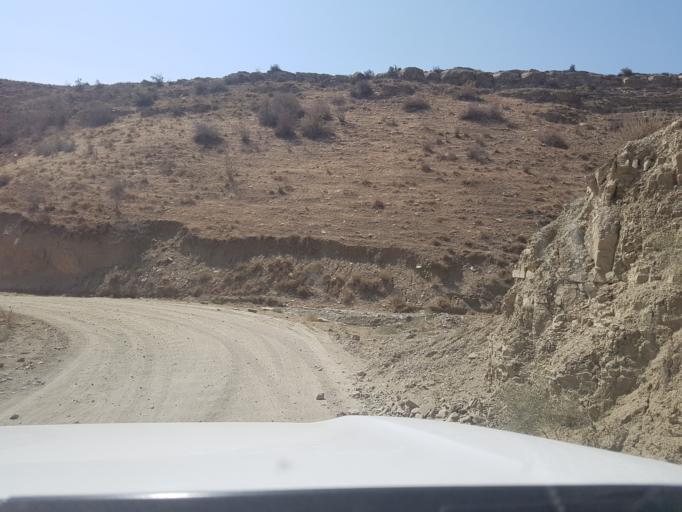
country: TM
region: Ahal
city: Baharly
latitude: 38.2405
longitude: 56.8896
